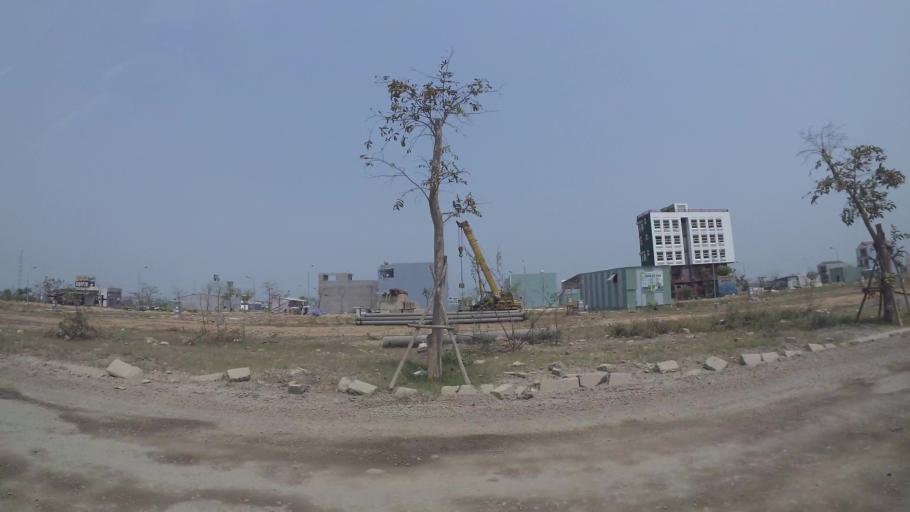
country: VN
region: Da Nang
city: Ngu Hanh Son
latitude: 16.0120
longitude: 108.2395
